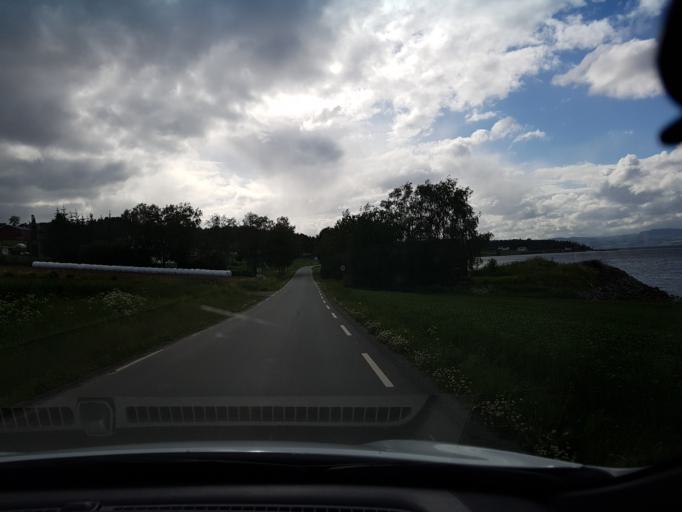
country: NO
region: Nord-Trondelag
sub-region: Frosta
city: Frosta
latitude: 63.6316
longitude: 10.8050
